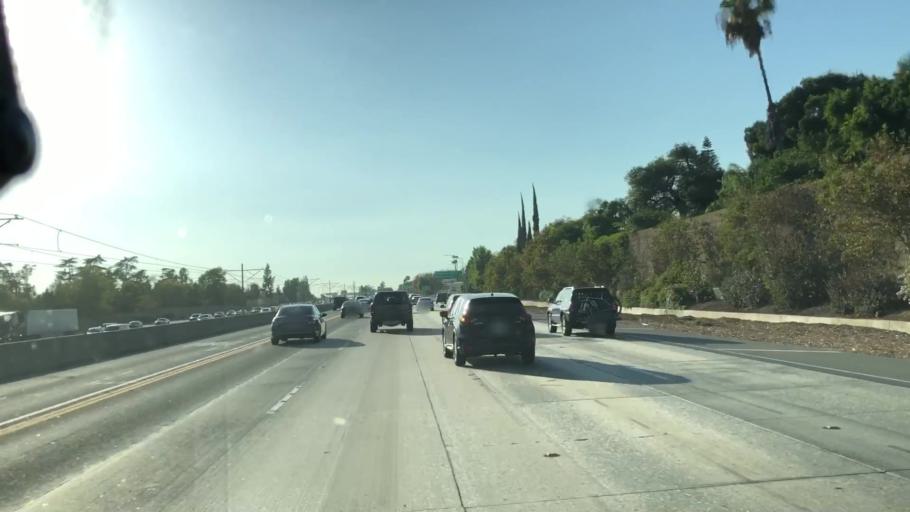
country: US
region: California
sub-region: Los Angeles County
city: Sierra Madre
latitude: 34.1471
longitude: -118.0616
